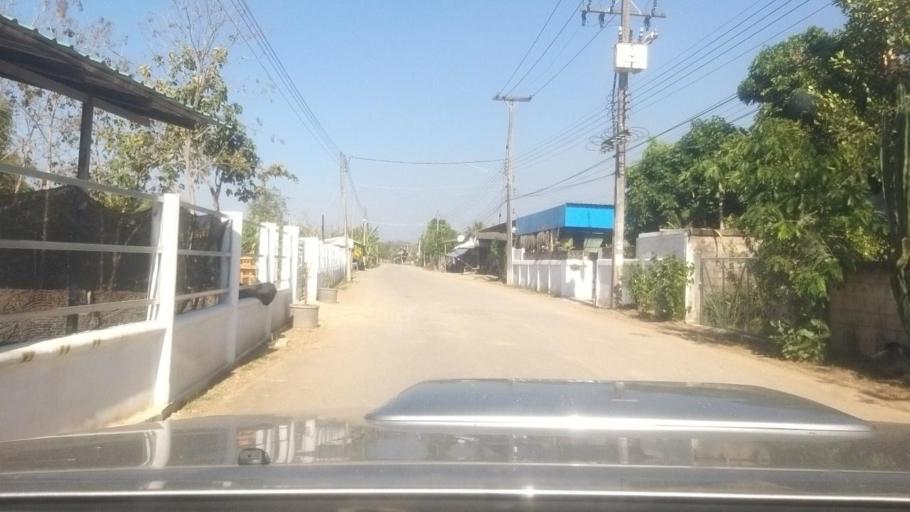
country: TH
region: Phrae
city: Nong Muang Khai
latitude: 18.2990
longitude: 100.0259
